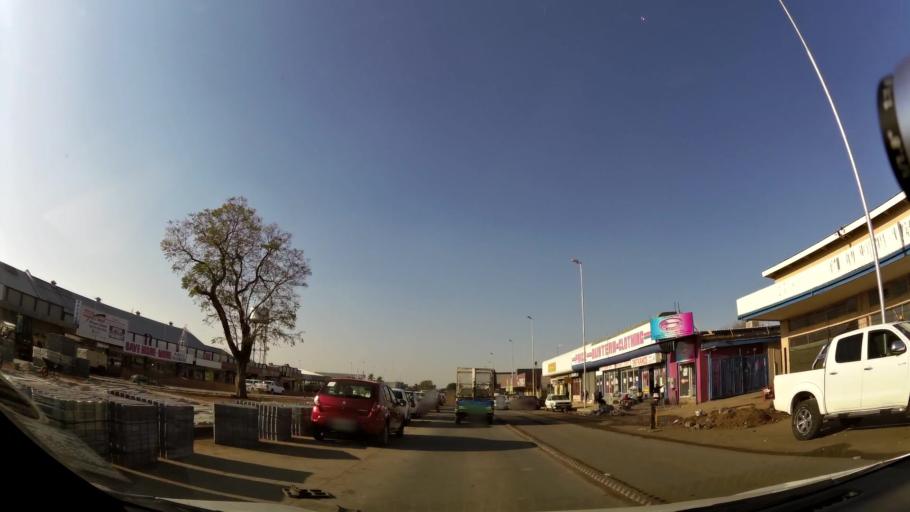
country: ZA
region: North-West
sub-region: Bojanala Platinum District Municipality
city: Rustenburg
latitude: -25.6663
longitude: 27.2414
